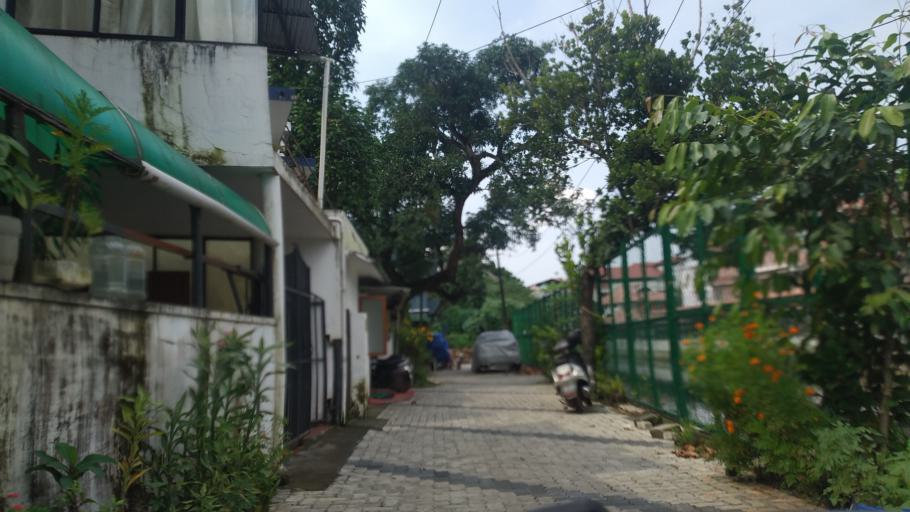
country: IN
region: Kerala
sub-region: Ernakulam
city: Cochin
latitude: 9.9785
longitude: 76.3024
